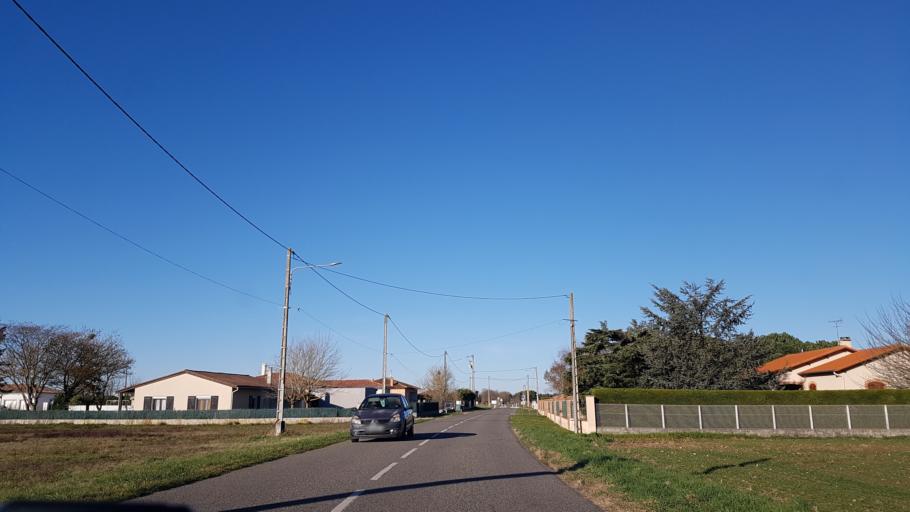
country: FR
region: Midi-Pyrenees
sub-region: Departement de la Haute-Garonne
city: Calmont
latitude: 43.2881
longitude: 1.6162
